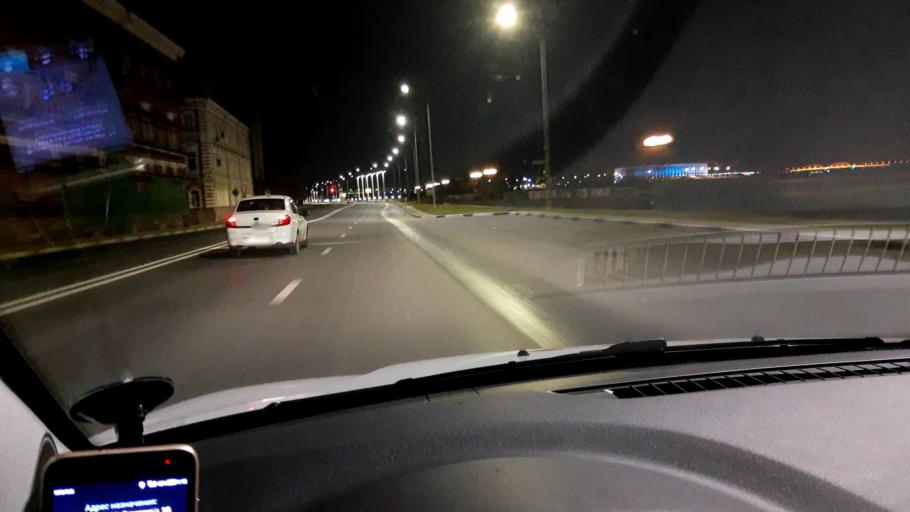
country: RU
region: Nizjnij Novgorod
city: Nizhniy Novgorod
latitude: 56.3321
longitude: 44.0020
